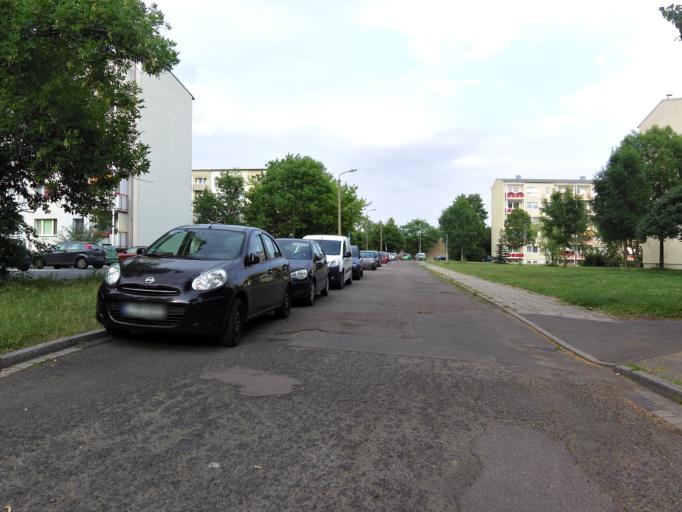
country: DE
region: Saxony
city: Markkleeberg
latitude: 51.3080
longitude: 12.3196
